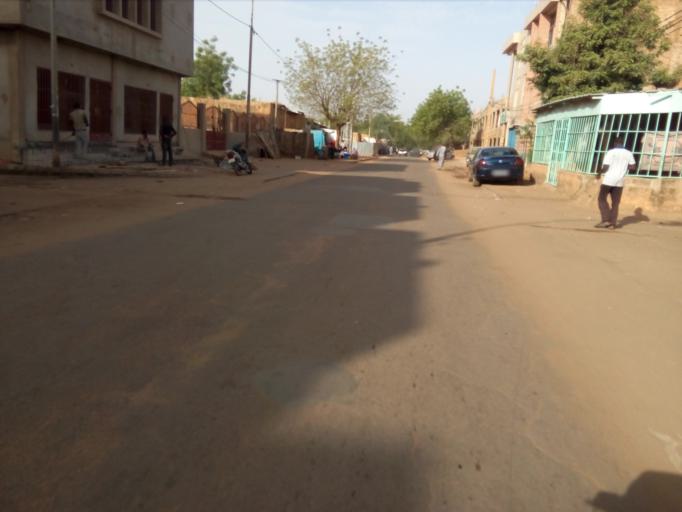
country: NE
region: Niamey
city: Niamey
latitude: 13.5137
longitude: 2.1243
